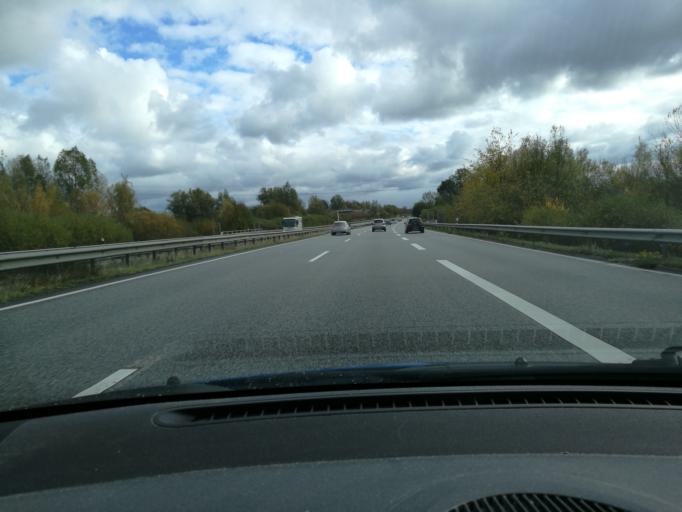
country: DE
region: Schleswig-Holstein
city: Krummesse
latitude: 53.8297
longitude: 10.6470
